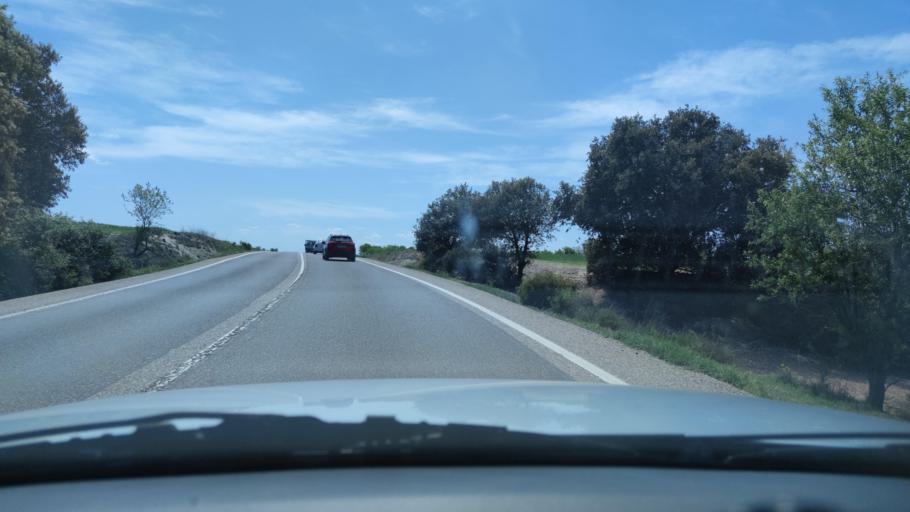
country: ES
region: Catalonia
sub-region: Provincia de Lleida
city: Tarrega
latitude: 41.6787
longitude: 1.1584
